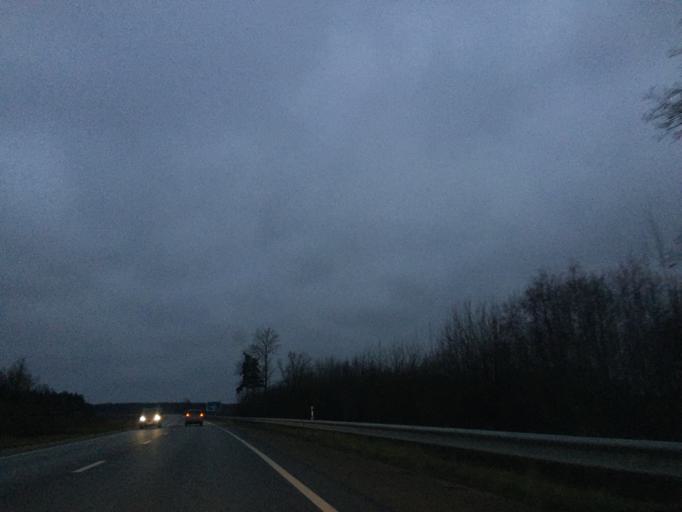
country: LV
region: Koceni
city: Koceni
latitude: 57.5318
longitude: 25.3699
